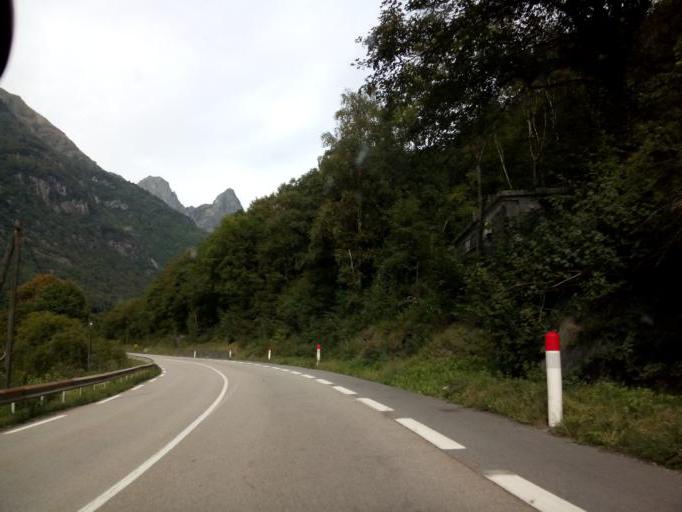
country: FR
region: Rhone-Alpes
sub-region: Departement de l'Isere
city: Livet-et-Gavet
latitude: 45.0979
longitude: 5.9152
